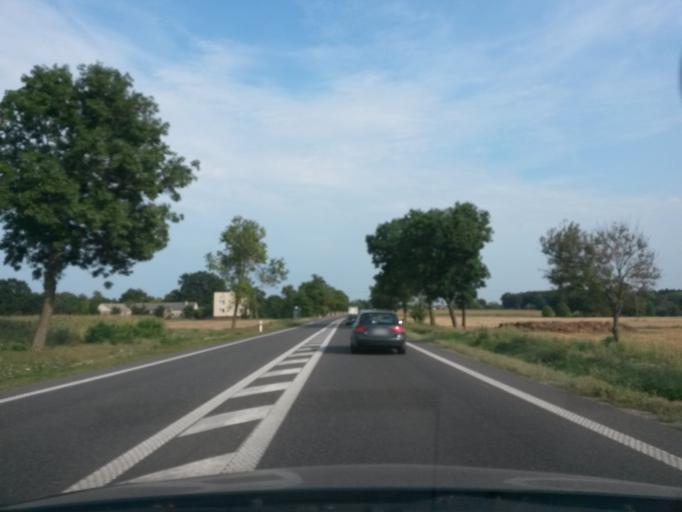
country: PL
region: Masovian Voivodeship
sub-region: Powiat sierpecki
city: Rosciszewo
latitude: 52.8348
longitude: 19.7426
